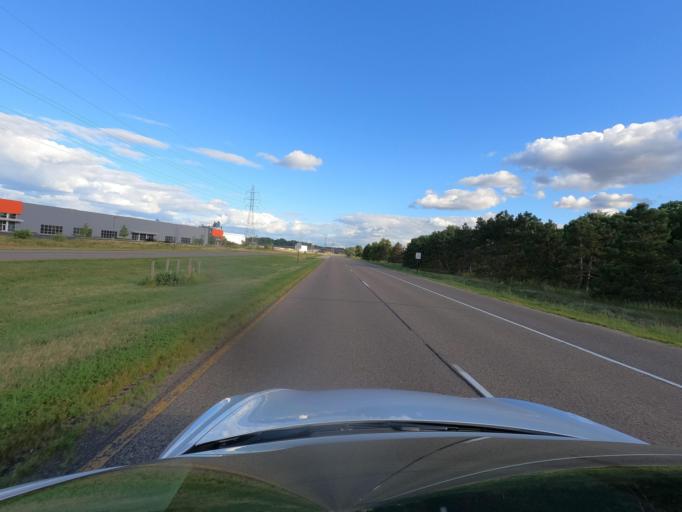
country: US
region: Minnesota
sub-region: Anoka County
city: Columbia Heights
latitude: 45.0539
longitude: -93.2788
